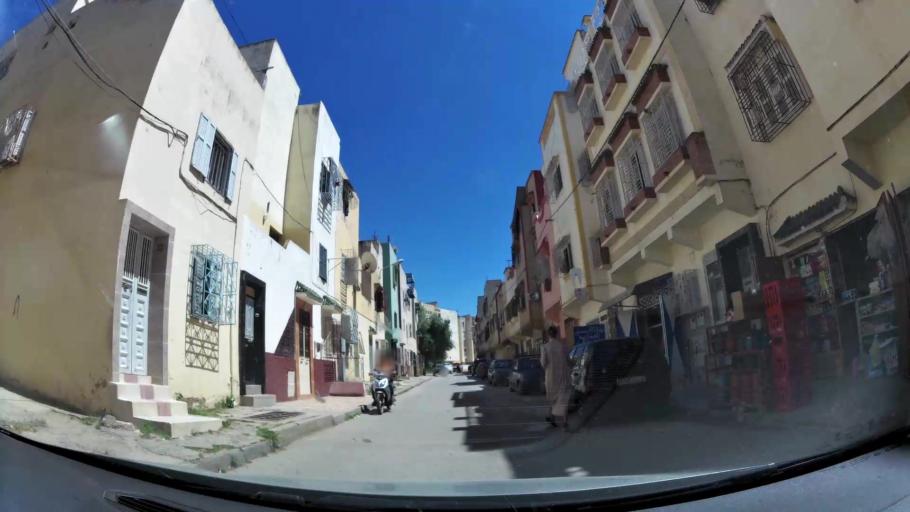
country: MA
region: Meknes-Tafilalet
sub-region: Meknes
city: Meknes
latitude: 33.9010
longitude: -5.5755
